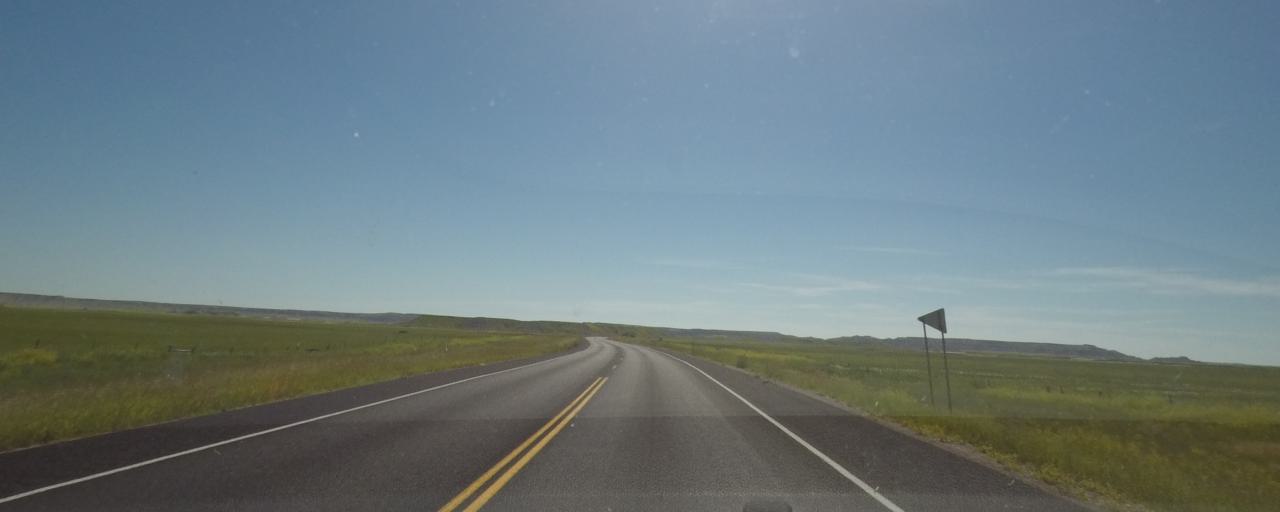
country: US
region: South Dakota
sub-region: Shannon County
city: Porcupine
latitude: 43.7784
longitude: -102.5432
